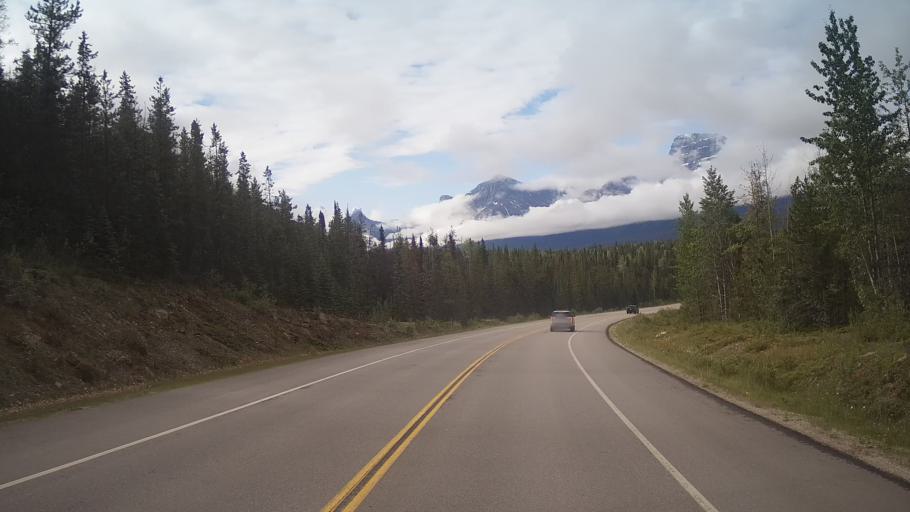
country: CA
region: Alberta
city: Jasper Park Lodge
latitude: 52.6856
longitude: -117.8657
